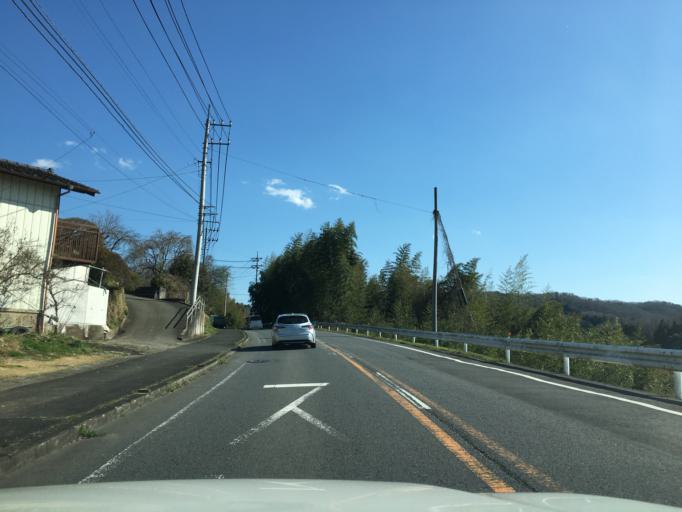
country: JP
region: Tochigi
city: Motegi
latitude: 36.5646
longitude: 140.2861
